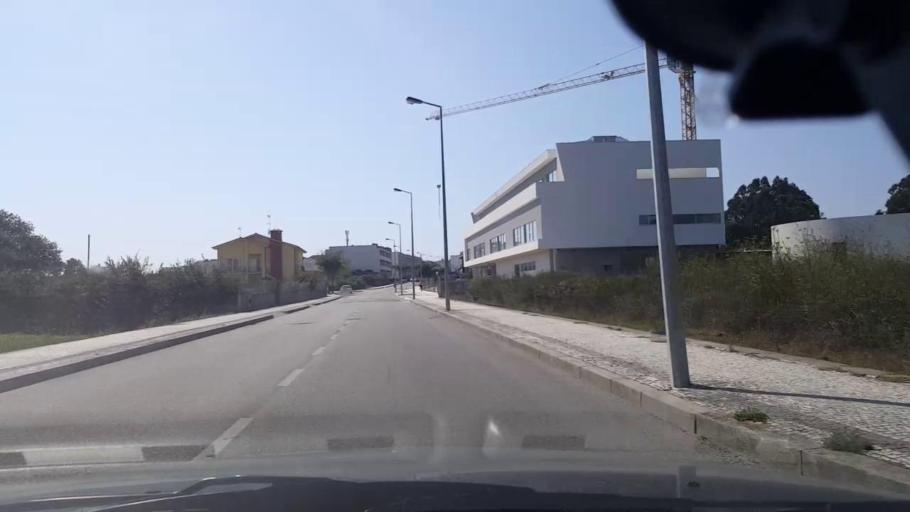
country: PT
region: Porto
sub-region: Vila do Conde
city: Vila do Conde
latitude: 41.3645
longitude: -8.7284
